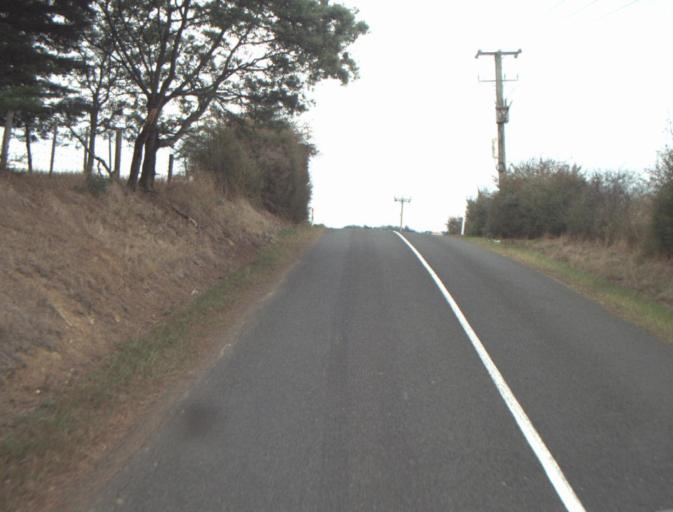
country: AU
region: Tasmania
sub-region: Northern Midlands
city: Evandale
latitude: -41.5159
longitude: 147.2157
